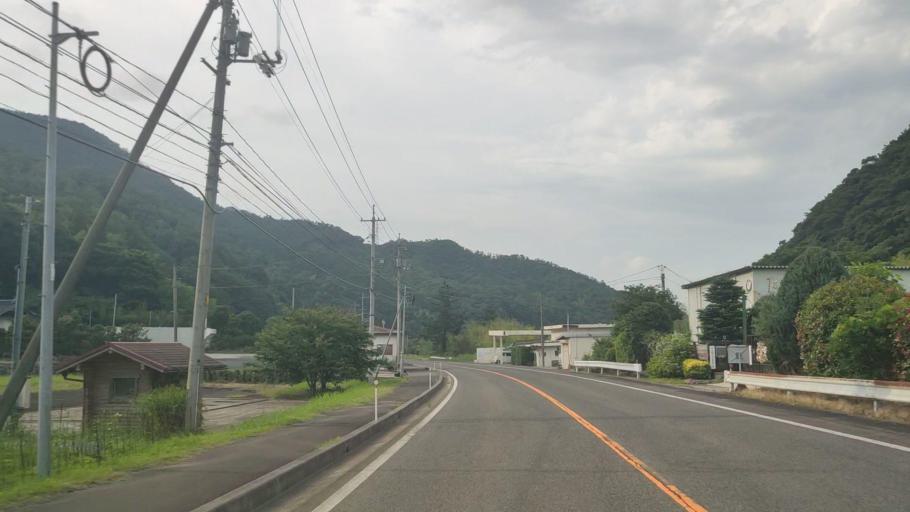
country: JP
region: Tottori
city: Kurayoshi
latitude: 35.3727
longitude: 133.8501
